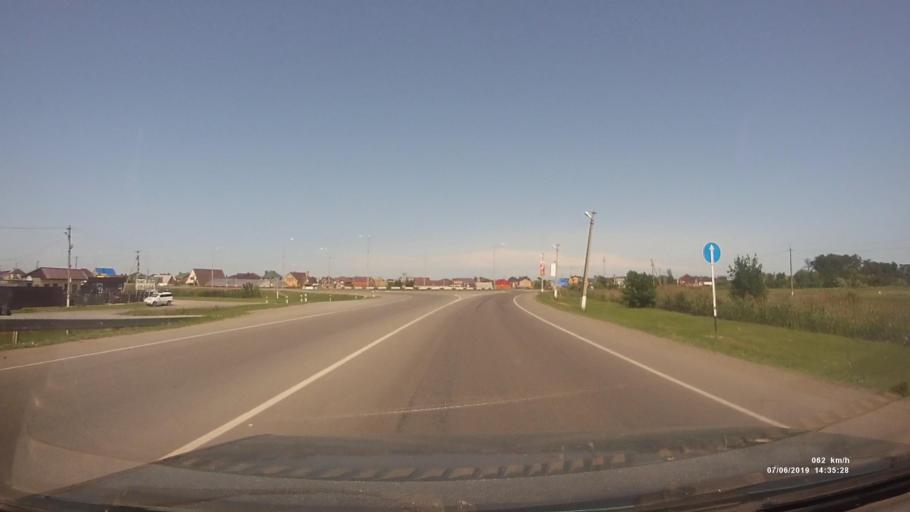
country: RU
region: Rostov
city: Bataysk
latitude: 47.1132
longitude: 39.6612
